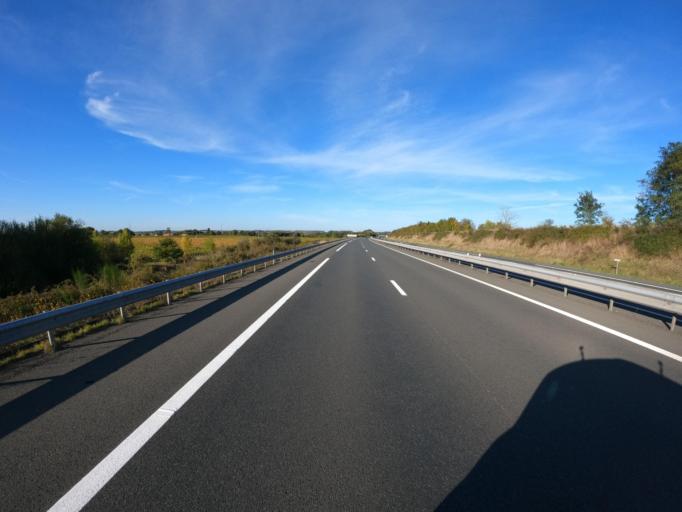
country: FR
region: Pays de la Loire
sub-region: Departement de Maine-et-Loire
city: Saint-Lambert-du-Lattay
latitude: 47.2894
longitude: -0.6151
